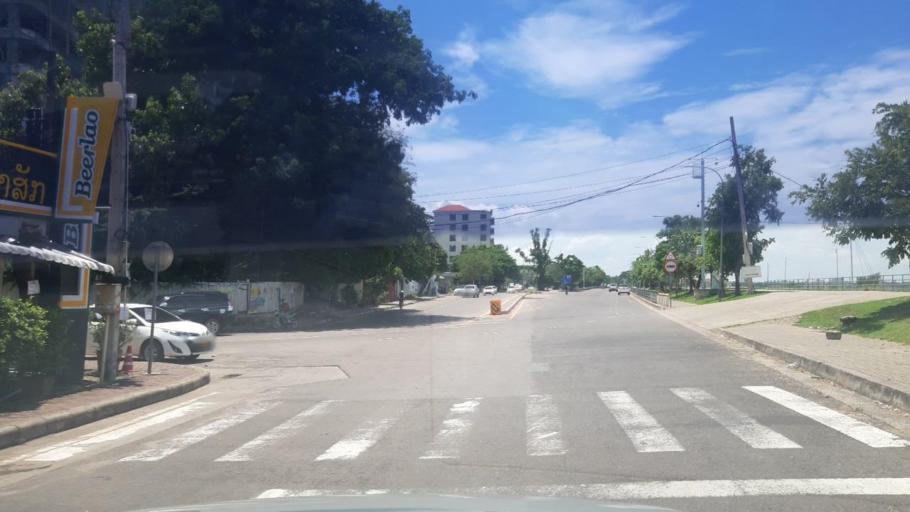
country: LA
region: Vientiane
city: Vientiane
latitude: 17.9650
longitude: 102.5990
